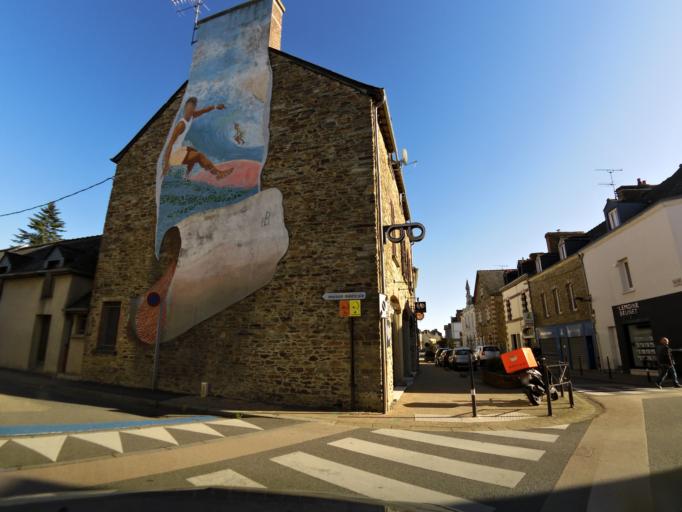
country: FR
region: Brittany
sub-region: Departement d'Ille-et-Vilaine
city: Bain-de-Bretagne
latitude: 47.8427
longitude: -1.6841
